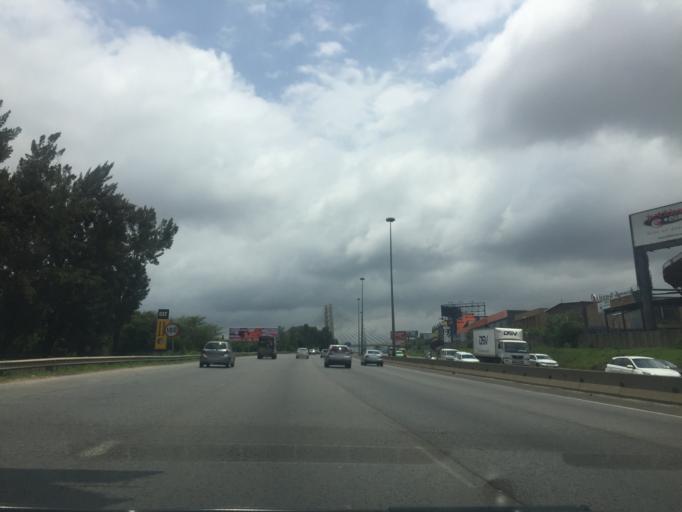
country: ZA
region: Gauteng
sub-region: City of Johannesburg Metropolitan Municipality
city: Modderfontein
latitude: -26.1022
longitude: 28.0786
